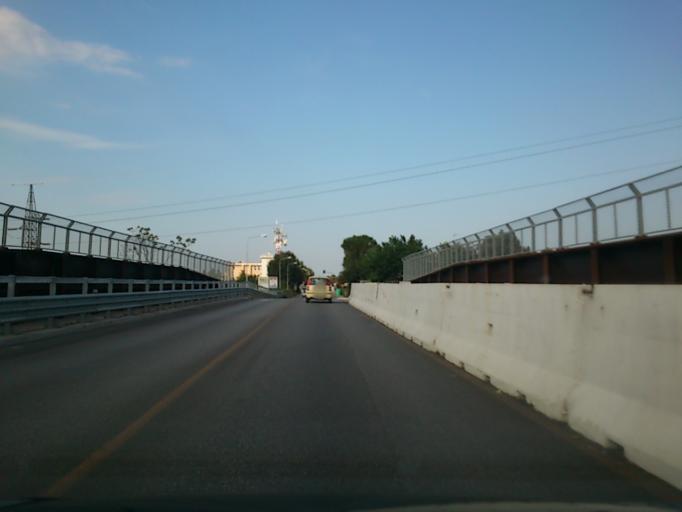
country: IT
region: The Marches
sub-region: Provincia di Pesaro e Urbino
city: Centinarola
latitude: 43.8281
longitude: 12.9961
